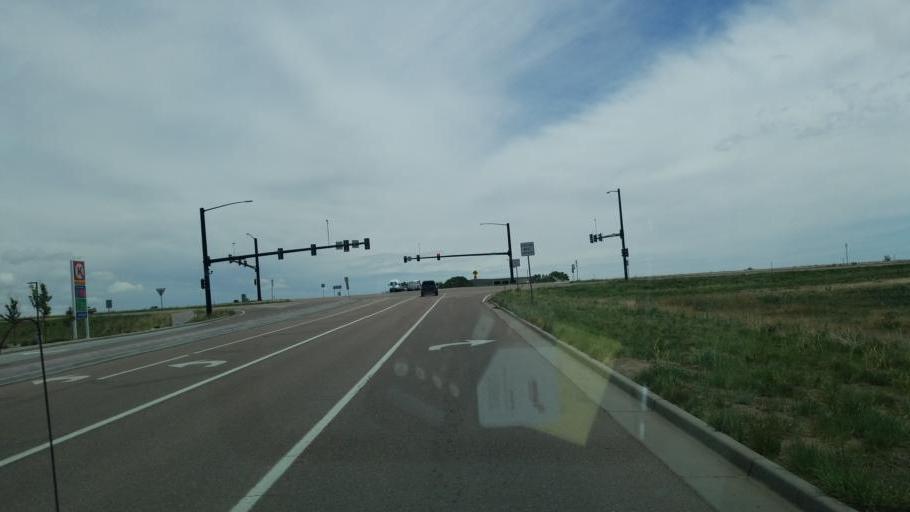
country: US
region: Colorado
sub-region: El Paso County
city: Cimarron Hills
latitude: 38.8440
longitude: -104.6921
